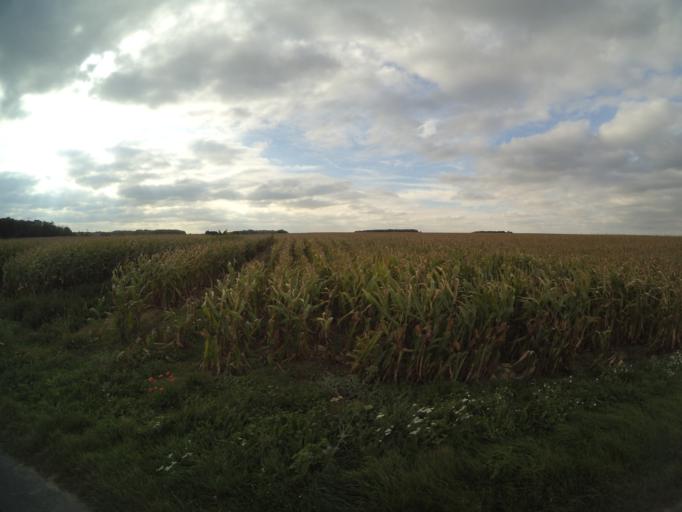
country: FR
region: Centre
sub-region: Departement d'Indre-et-Loire
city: Nazelles-Negron
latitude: 47.4734
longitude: 0.9430
